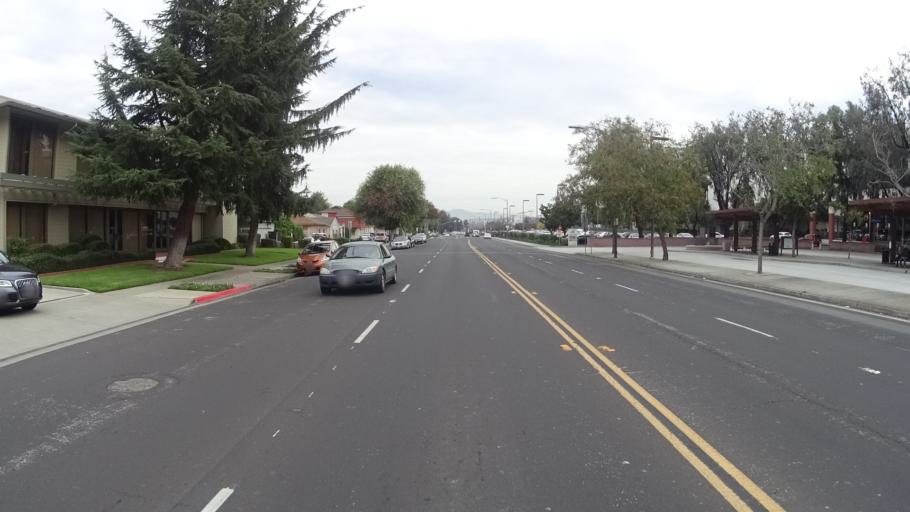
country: US
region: California
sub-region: Santa Clara County
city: Burbank
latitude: 37.3270
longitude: -121.9481
